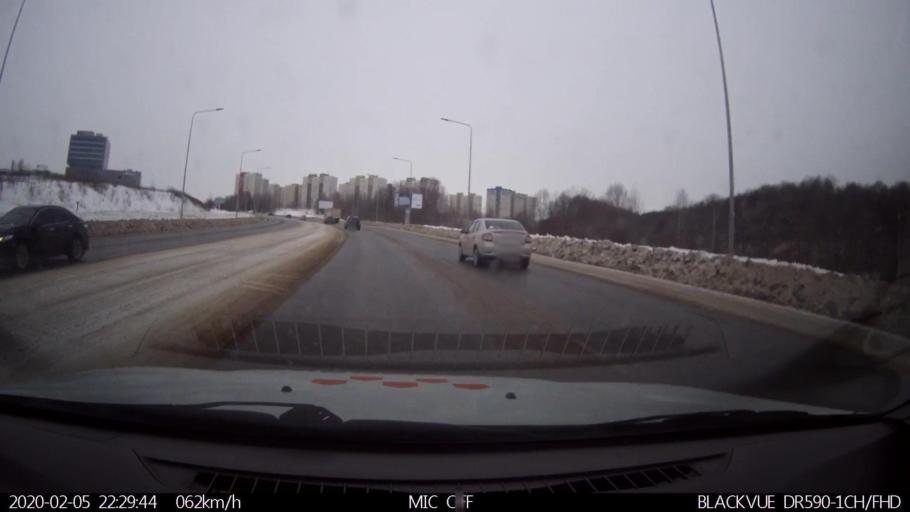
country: RU
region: Nizjnij Novgorod
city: Imeni Stepana Razina
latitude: 54.7472
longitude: 44.1481
